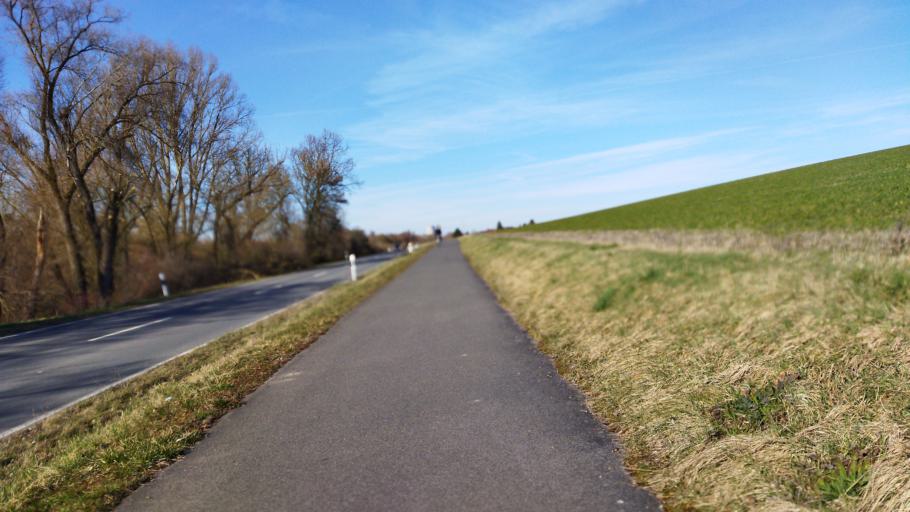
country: DE
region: Bavaria
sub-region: Regierungsbezirk Unterfranken
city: Wipfeld
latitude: 49.9347
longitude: 10.1825
